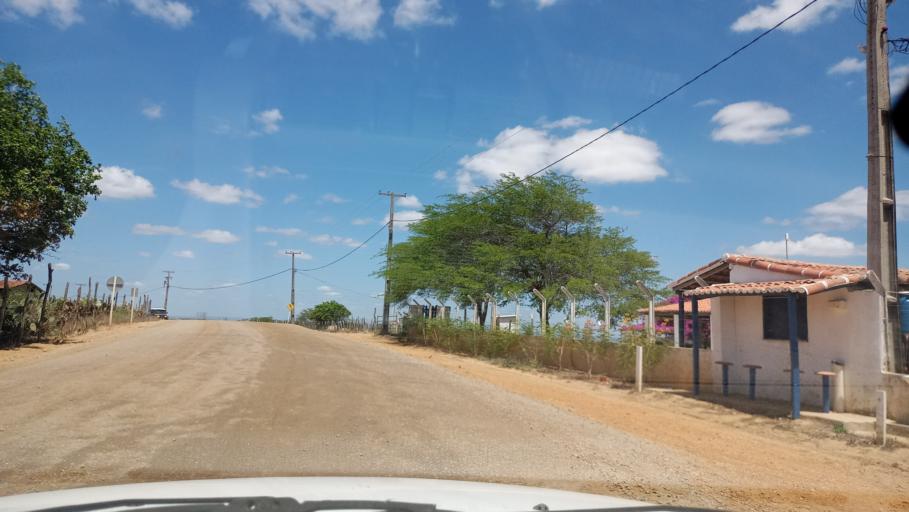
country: BR
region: Rio Grande do Norte
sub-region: Sao Paulo Do Potengi
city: Sao Paulo do Potengi
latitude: -5.7815
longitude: -35.9142
